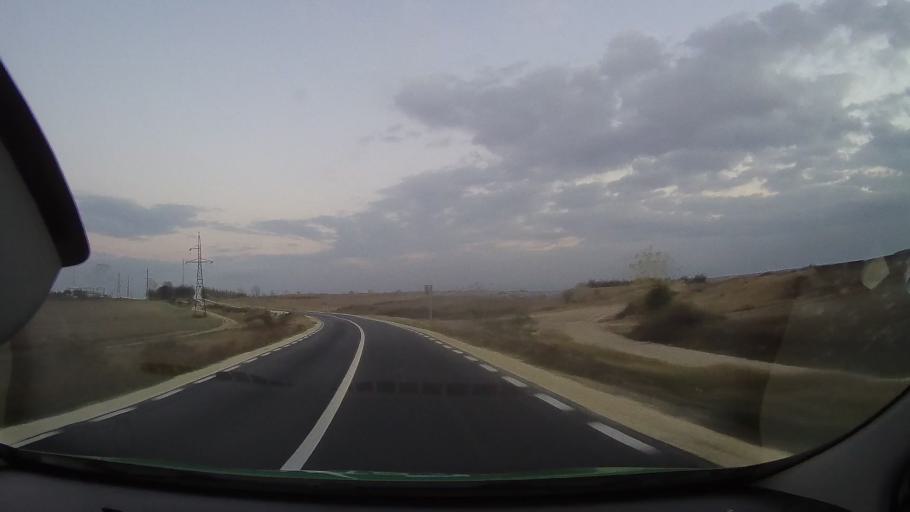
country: RO
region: Constanta
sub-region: Comuna Baneasa
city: Baneasa
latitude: 44.0810
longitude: 27.6892
